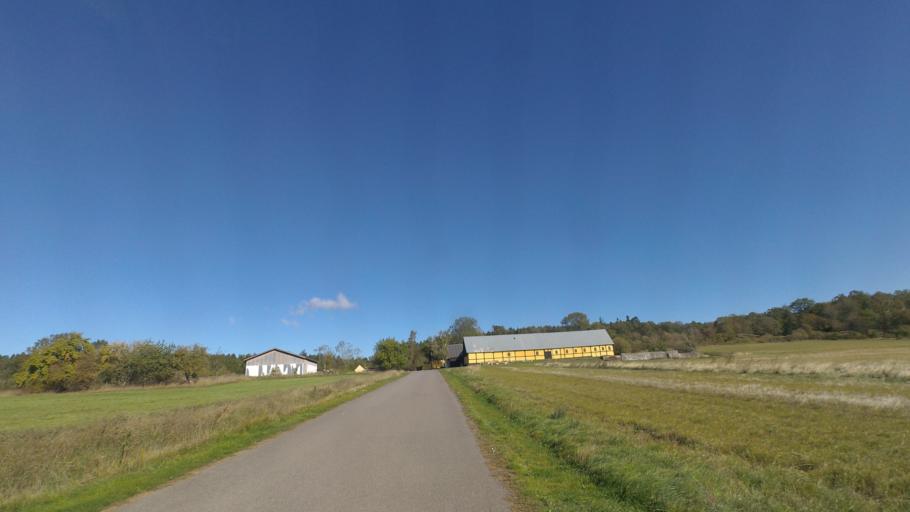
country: DK
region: Capital Region
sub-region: Bornholm Kommune
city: Nexo
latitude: 55.0791
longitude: 15.1009
